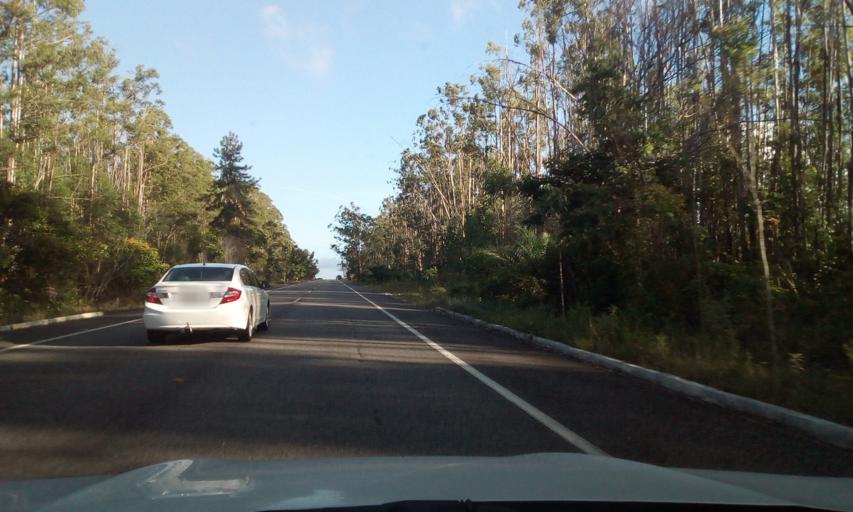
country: BR
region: Bahia
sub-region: Entre Rios
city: Entre Rios
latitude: -12.3225
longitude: -37.9043
